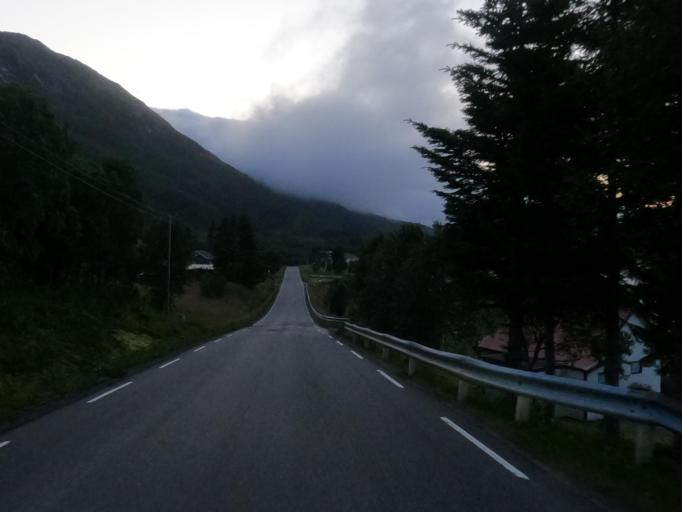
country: NO
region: Nordland
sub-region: Lodingen
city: Lodingen
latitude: 68.5670
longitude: 15.8001
